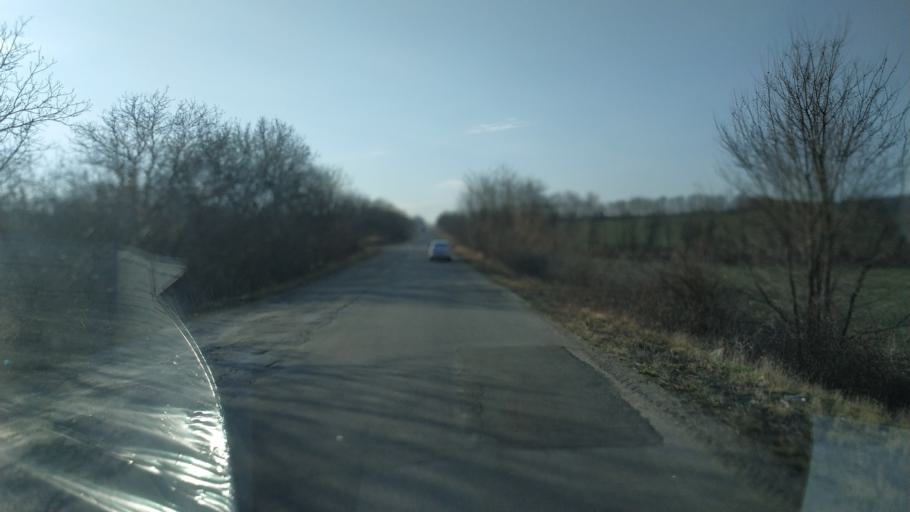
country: MD
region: Chisinau
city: Singera
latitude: 46.8784
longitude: 29.0394
